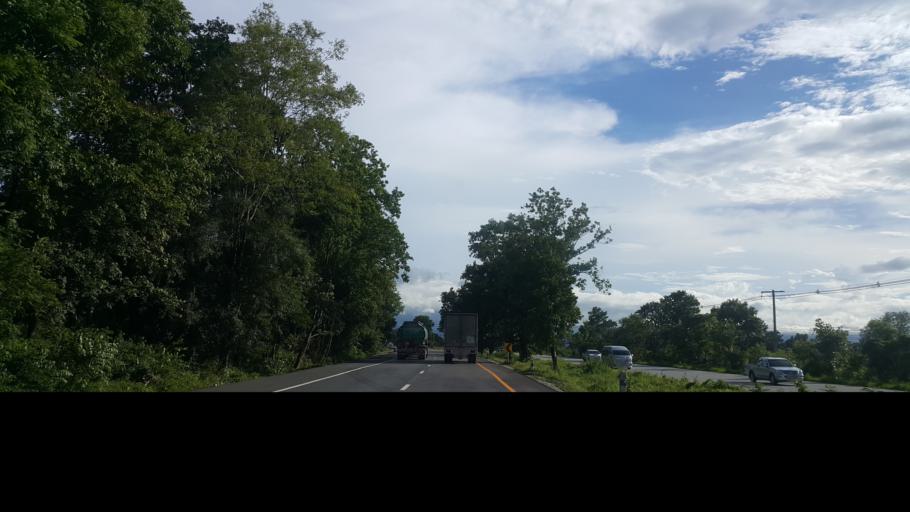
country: TH
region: Tak
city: Ban Tak
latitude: 17.1264
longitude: 99.0993
